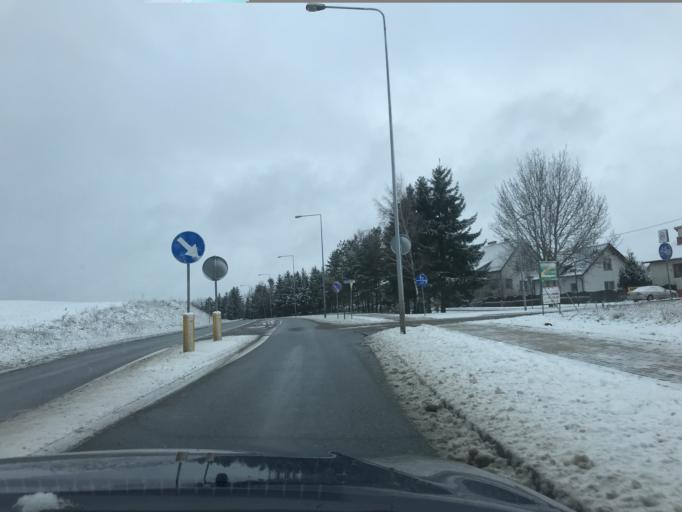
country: PL
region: Pomeranian Voivodeship
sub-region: Powiat bytowski
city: Bytow
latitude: 54.1878
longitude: 17.5095
